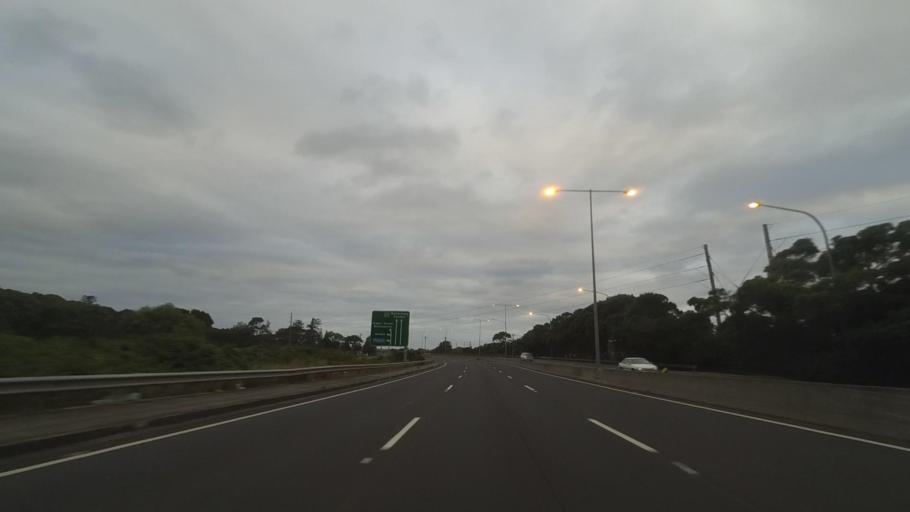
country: AU
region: New South Wales
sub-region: Kiama
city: Kiama
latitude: -34.6618
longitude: 150.8507
